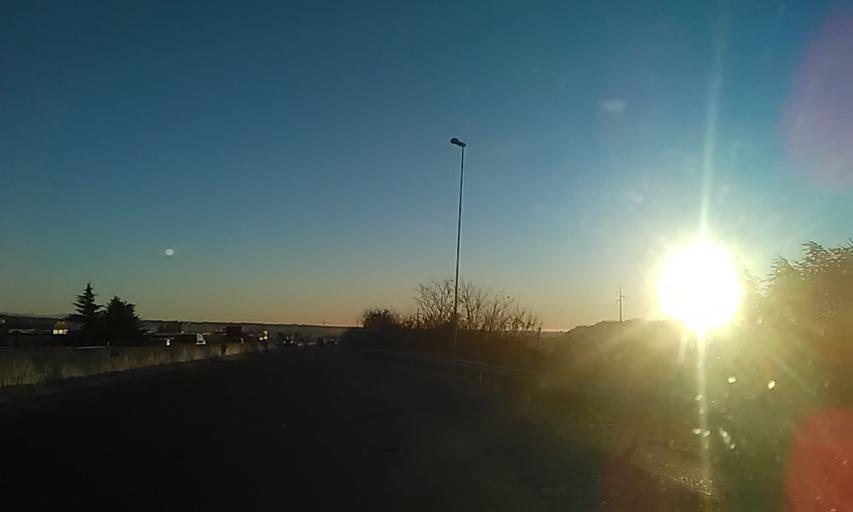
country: IT
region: Piedmont
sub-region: Provincia di Biella
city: Vigliano Biellese
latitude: 45.5554
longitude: 8.1148
